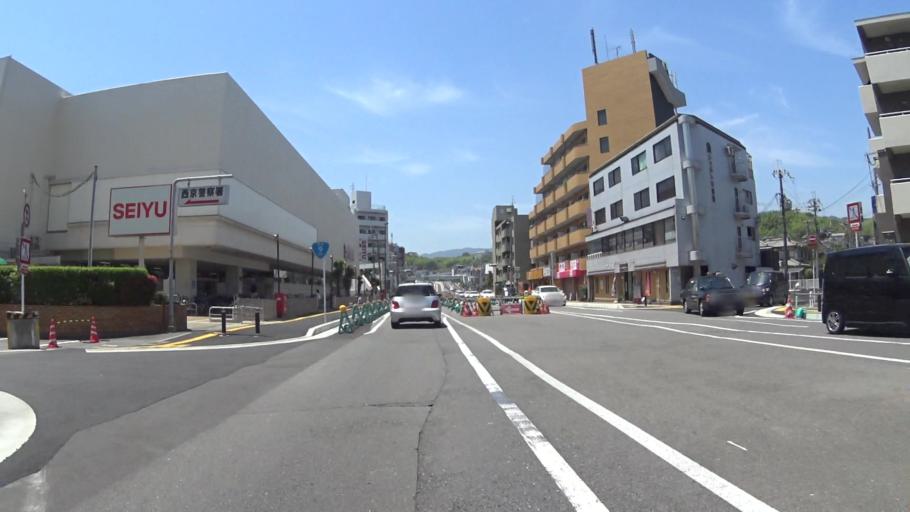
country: JP
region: Kyoto
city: Muko
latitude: 34.9813
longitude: 135.6921
